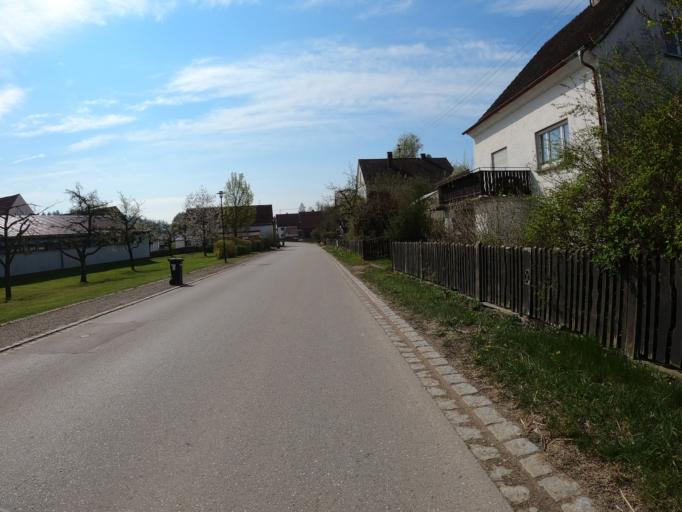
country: DE
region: Bavaria
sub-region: Swabia
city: Pfaffenhofen an der Roth
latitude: 48.3835
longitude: 10.1930
